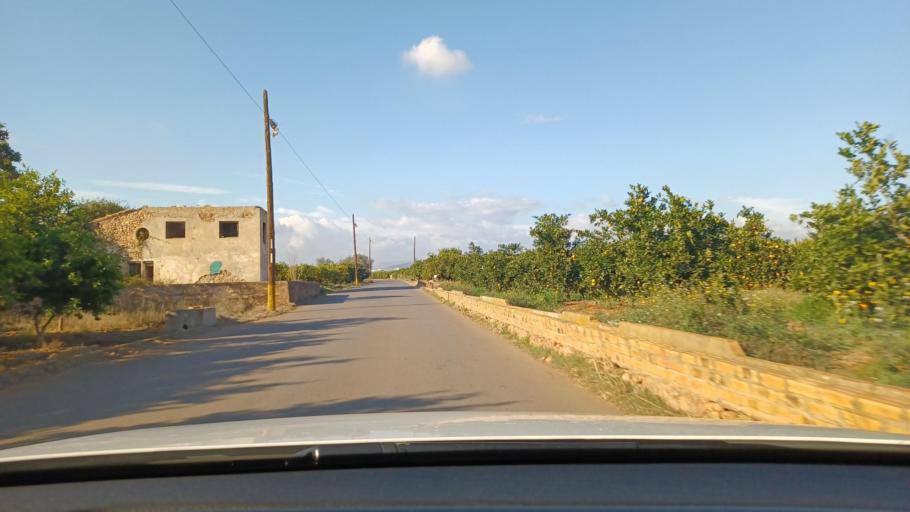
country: ES
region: Valencia
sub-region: Provincia de Castello
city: Betxi
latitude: 39.9392
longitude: -0.2102
